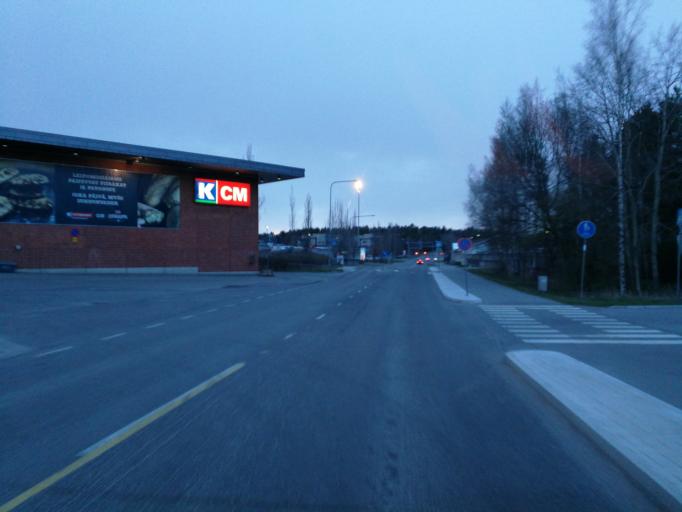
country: FI
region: Varsinais-Suomi
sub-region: Turku
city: Turku
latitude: 60.4716
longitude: 22.2347
